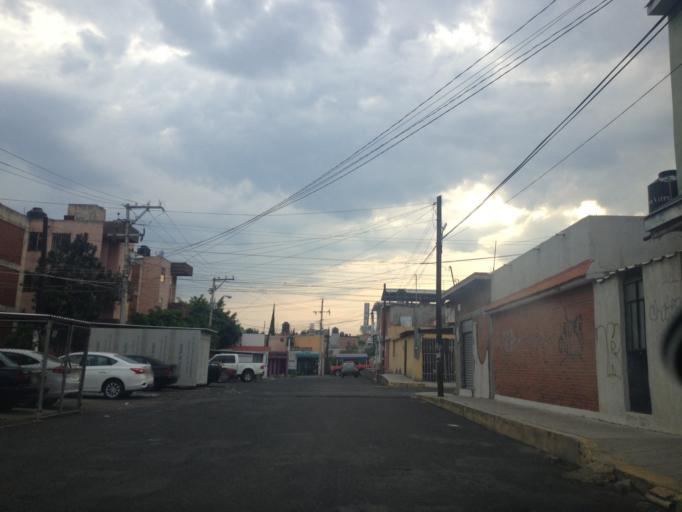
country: MX
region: Michoacan
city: Morelia
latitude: 19.7058
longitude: -101.2347
